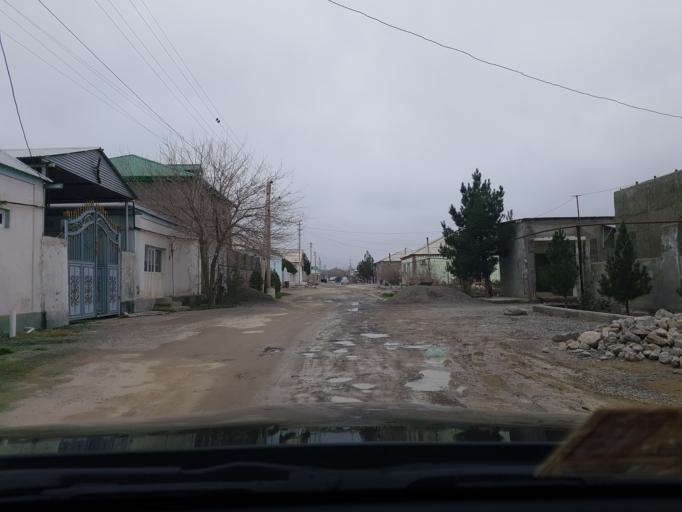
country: TM
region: Ahal
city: Abadan
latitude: 38.1437
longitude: 57.9485
